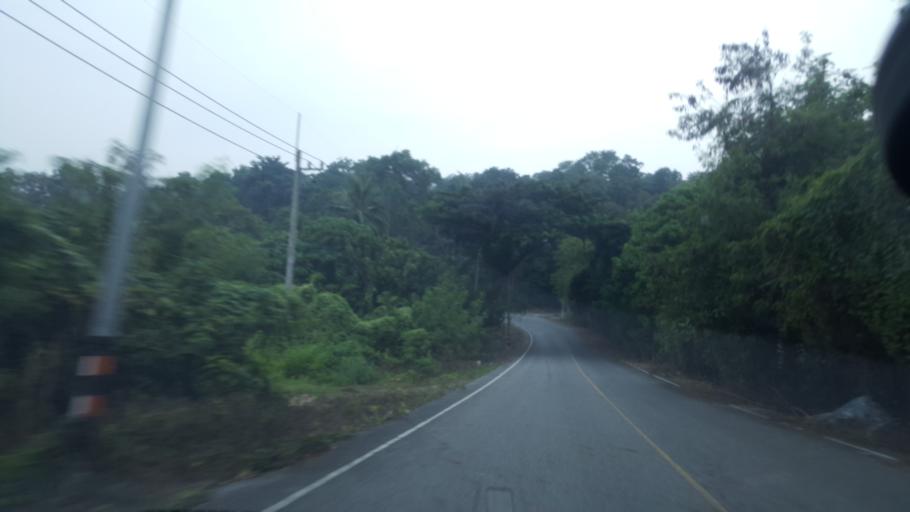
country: TH
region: Chon Buri
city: Ban Bueng
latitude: 13.2372
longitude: 101.0310
